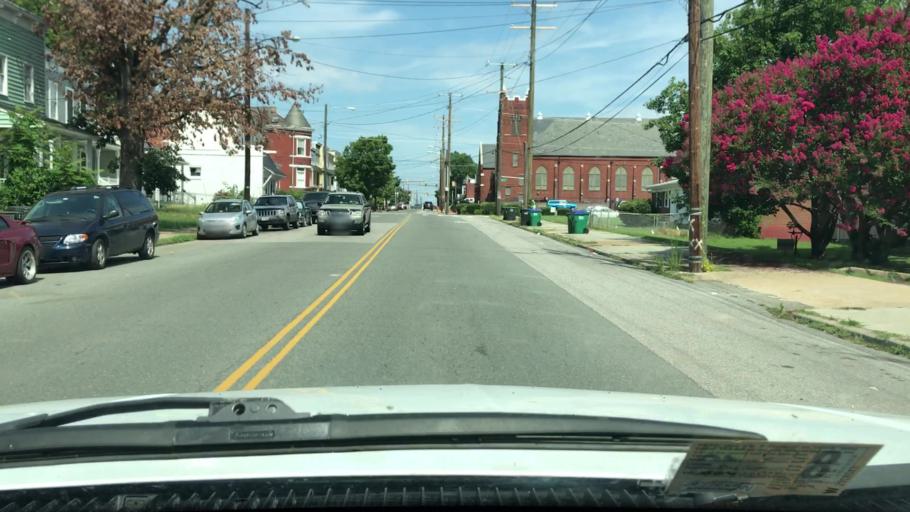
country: US
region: Virginia
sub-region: City of Richmond
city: Richmond
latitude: 37.5554
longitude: -77.4508
